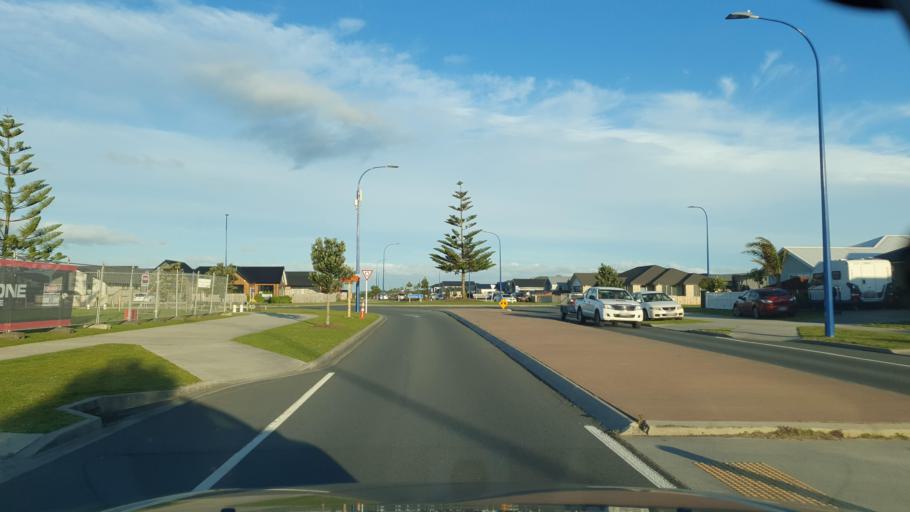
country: NZ
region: Bay of Plenty
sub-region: Western Bay of Plenty District
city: Maketu
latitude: -37.7251
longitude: 176.3404
